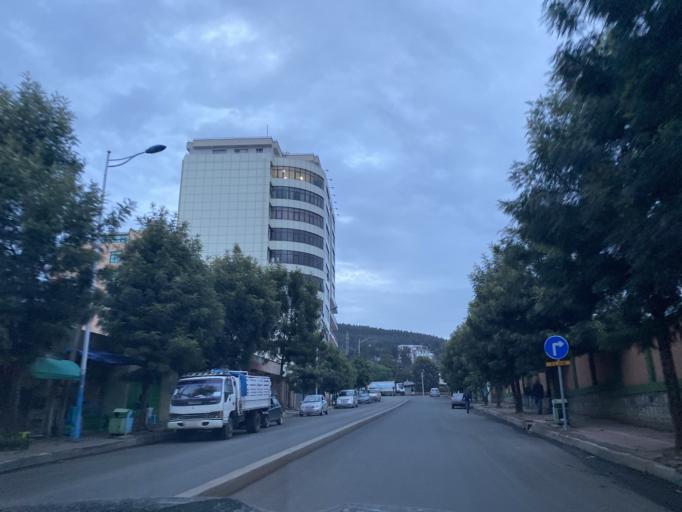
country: ET
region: Adis Abeba
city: Addis Ababa
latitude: 9.0188
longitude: 38.8114
